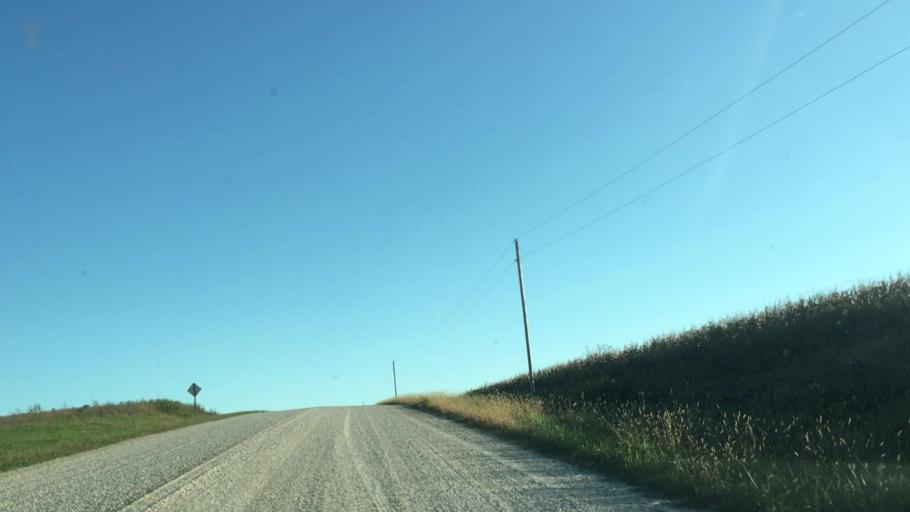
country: US
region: Minnesota
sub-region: Fillmore County
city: Chatfield
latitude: 43.8170
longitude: -92.0395
